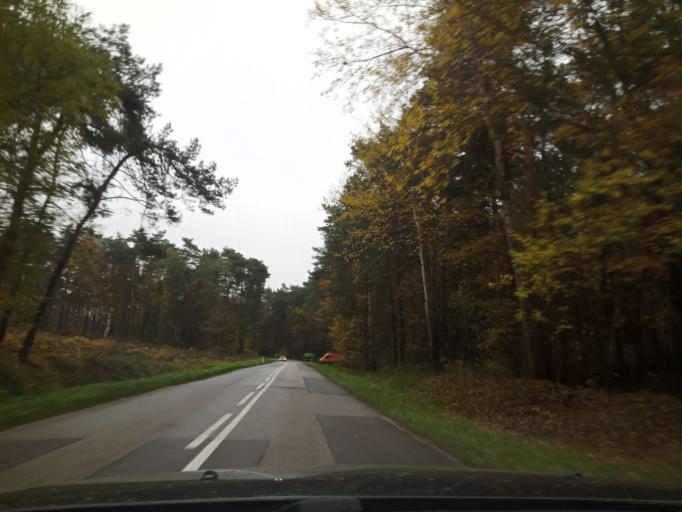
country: PL
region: Swietokrzyskie
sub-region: Powiat pinczowski
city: Dzialoszyce
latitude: 50.4550
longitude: 20.3621
